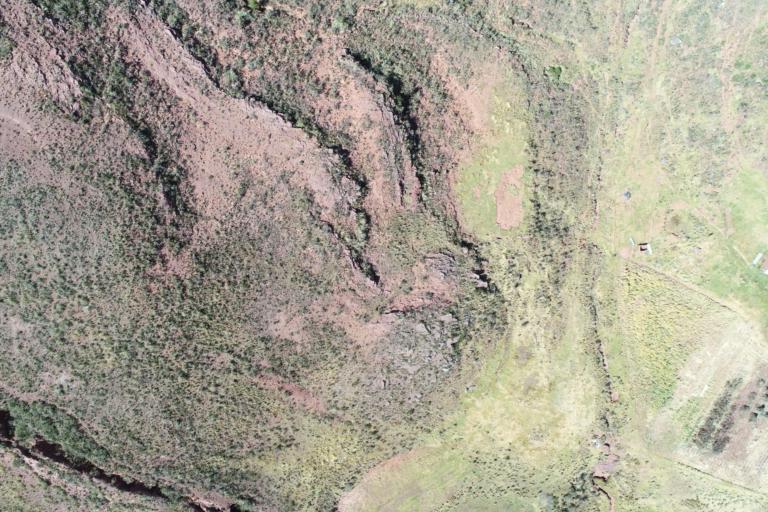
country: BO
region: La Paz
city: Tiahuanaco
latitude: -16.5962
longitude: -68.7594
